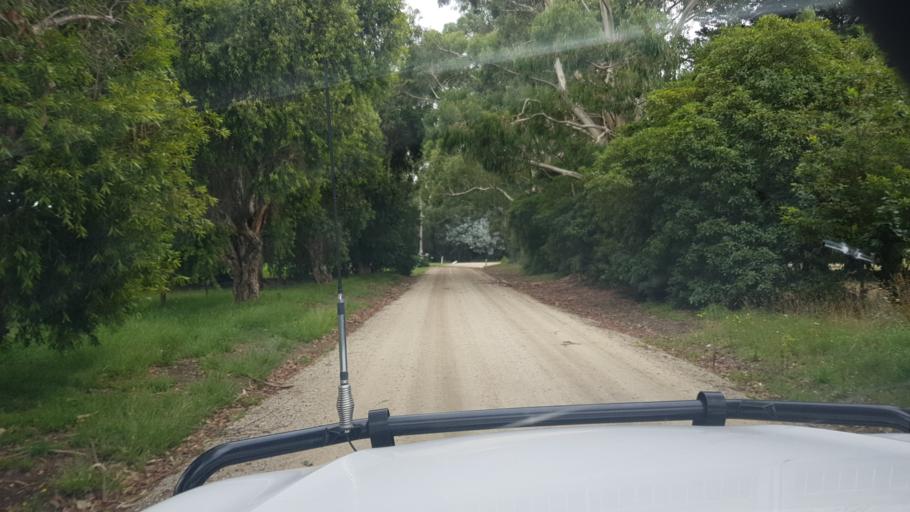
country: AU
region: Victoria
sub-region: Baw Baw
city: Warragul
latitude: -38.1177
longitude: 146.0072
